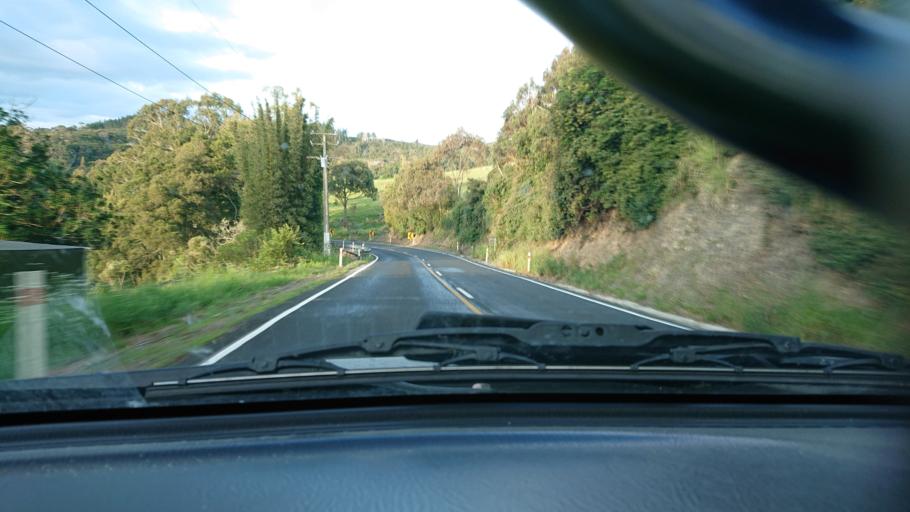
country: NZ
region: Auckland
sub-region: Auckland
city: Parakai
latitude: -36.5364
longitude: 174.4565
